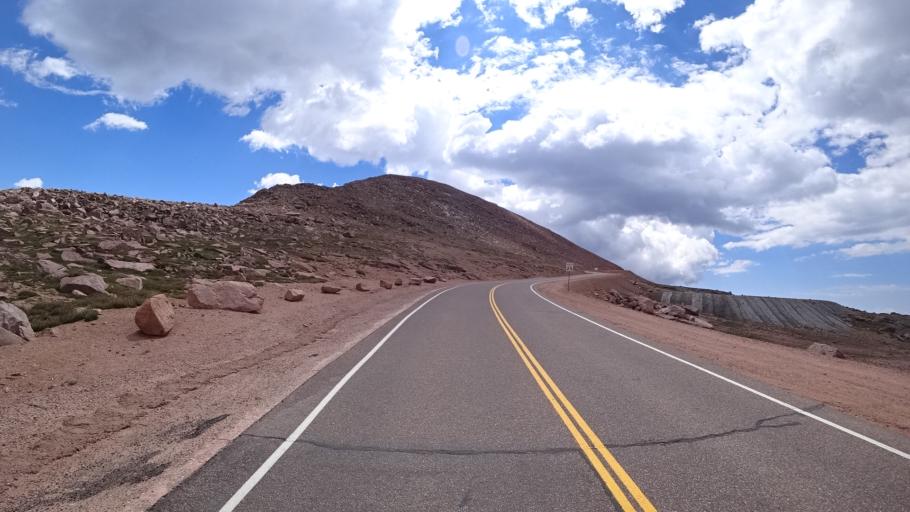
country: US
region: Colorado
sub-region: El Paso County
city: Cascade-Chipita Park
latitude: 38.8456
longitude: -105.0511
